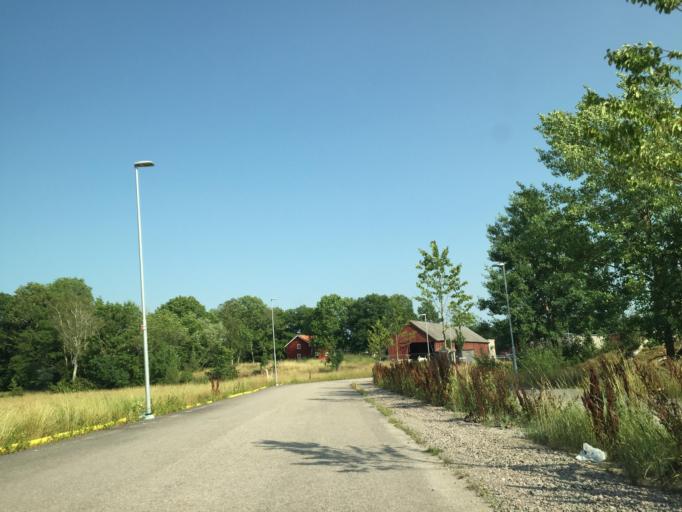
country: SE
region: Vaestra Goetaland
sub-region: Vanersborgs Kommun
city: Vanersborg
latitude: 58.3708
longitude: 12.3524
